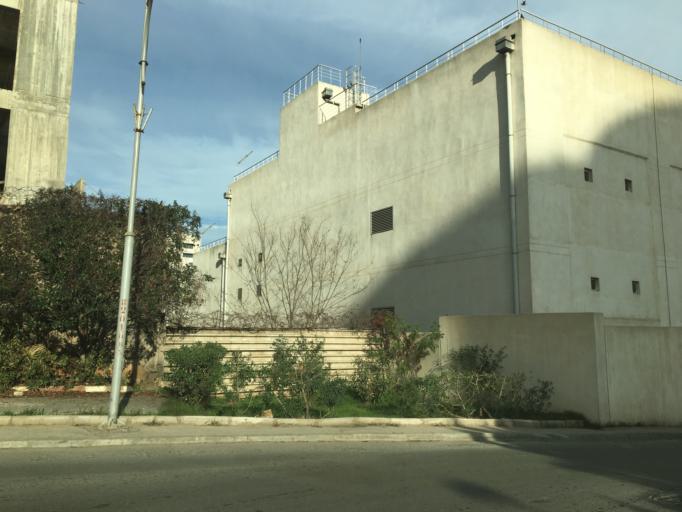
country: DZ
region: Alger
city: Birkhadem
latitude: 36.7410
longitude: 3.0864
